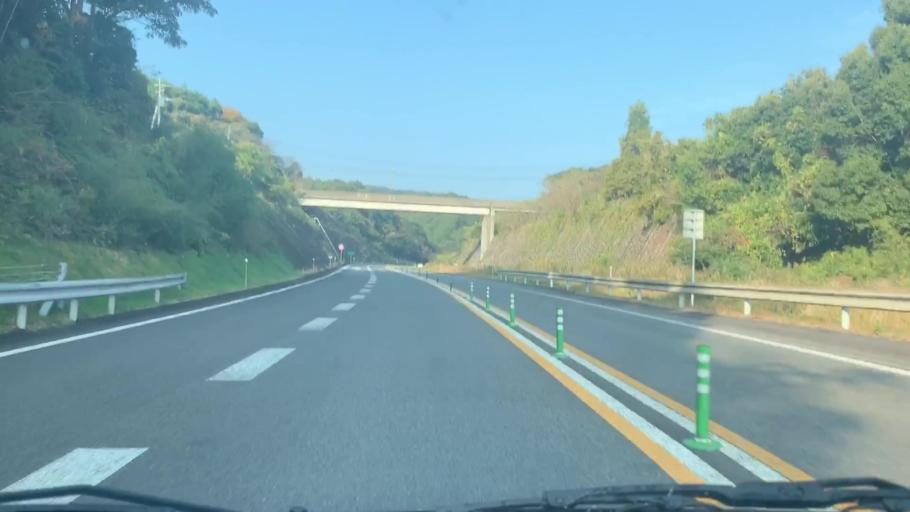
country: JP
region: Saga Prefecture
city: Imaricho-ko
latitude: 33.1591
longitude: 129.8700
